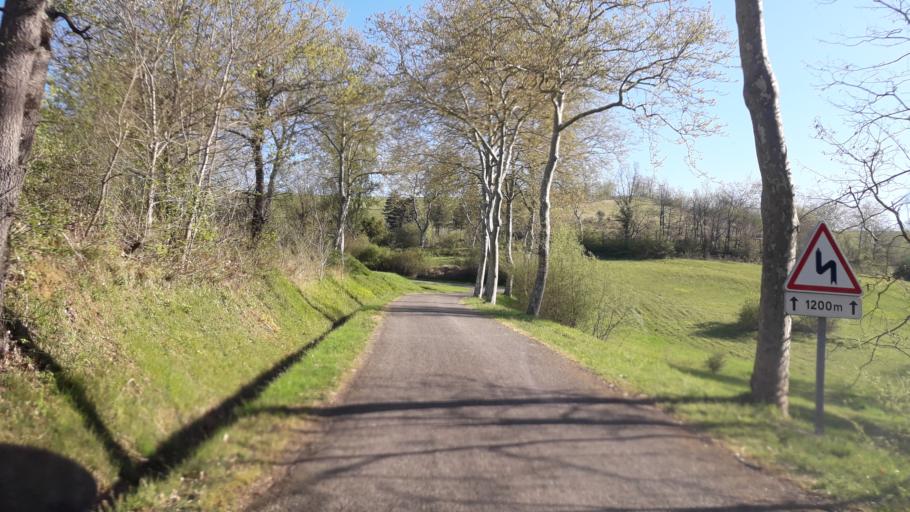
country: FR
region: Midi-Pyrenees
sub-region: Departement de la Haute-Garonne
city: Montesquieu-Volvestre
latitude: 43.2011
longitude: 1.2698
